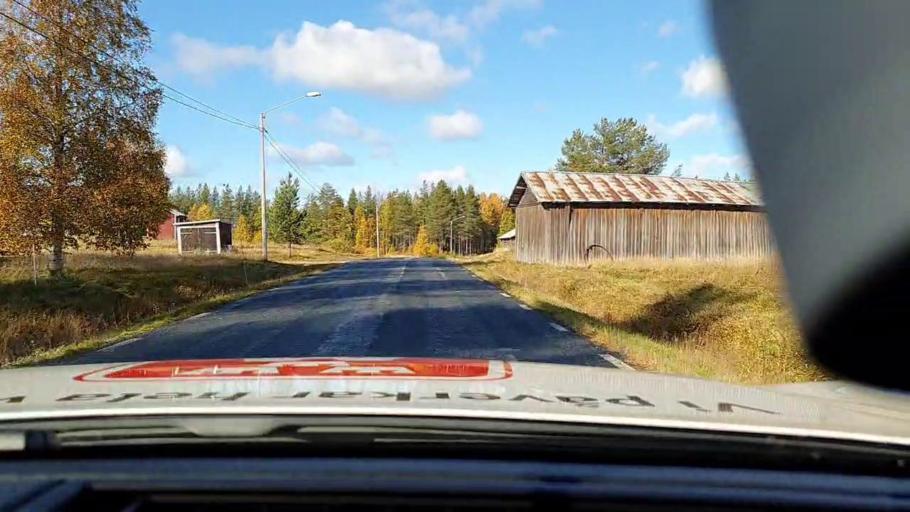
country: SE
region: Vaesterbotten
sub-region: Skelleftea Kommun
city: Langsele
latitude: 65.0119
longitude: 20.0822
